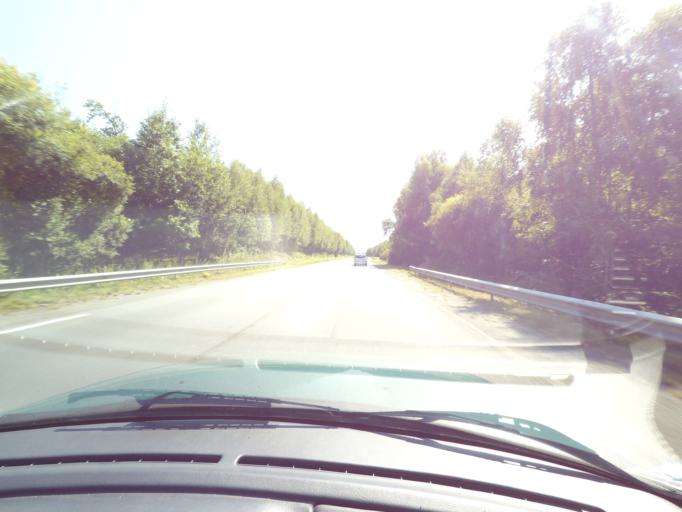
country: FR
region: Limousin
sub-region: Departement de la Haute-Vienne
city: Chaptelat
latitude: 45.8913
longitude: 1.2581
